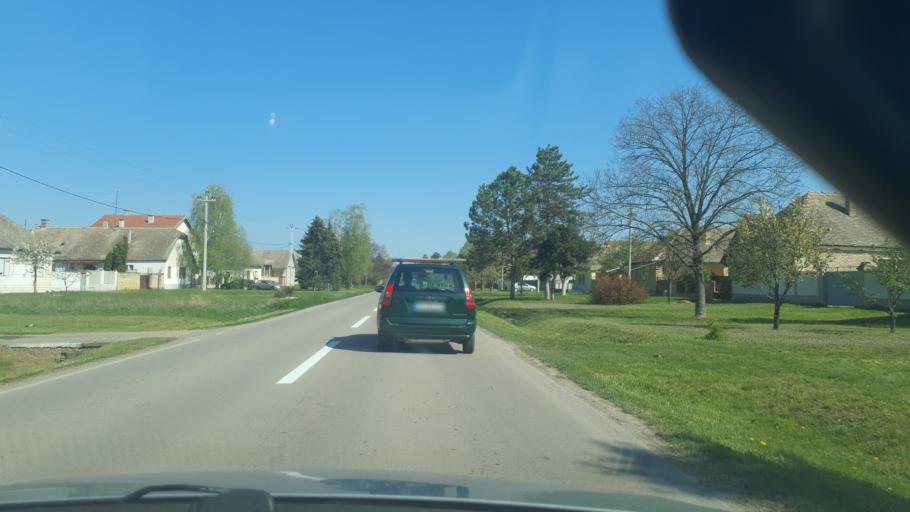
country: RS
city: Kolut
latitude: 45.8503
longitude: 18.9335
